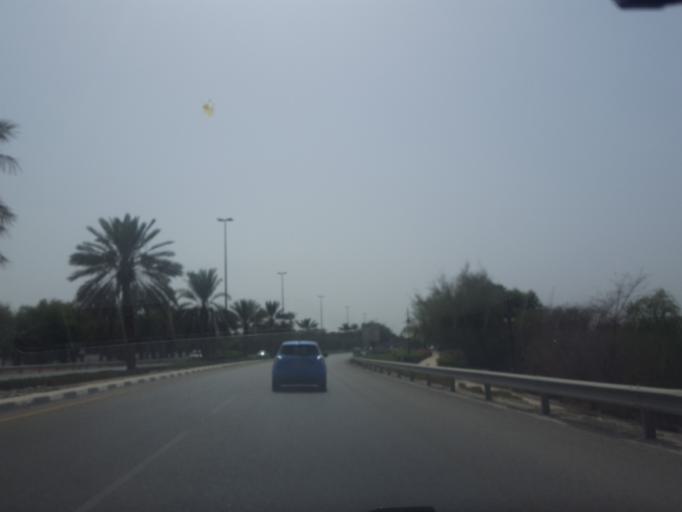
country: AE
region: Abu Dhabi
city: Al Ain
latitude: 24.2054
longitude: 55.8043
